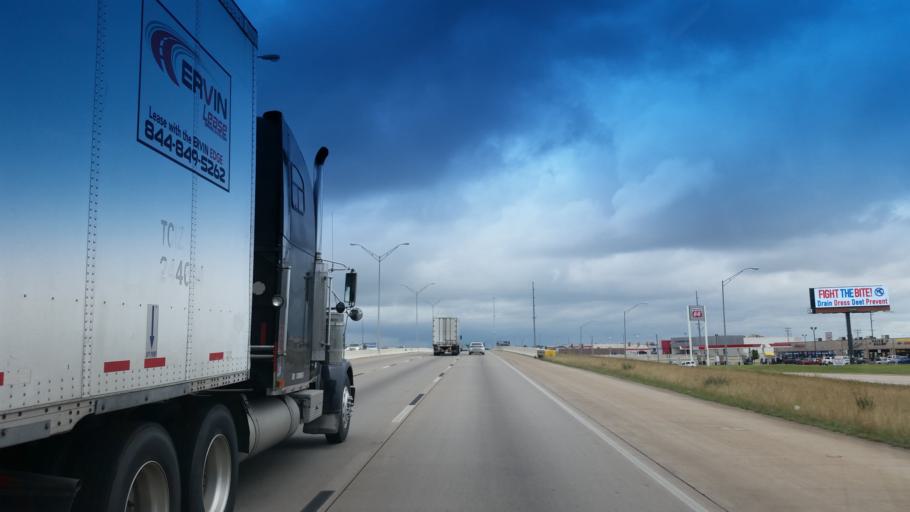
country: US
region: Oklahoma
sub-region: Oklahoma County
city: Del City
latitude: 35.4228
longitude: -97.4874
